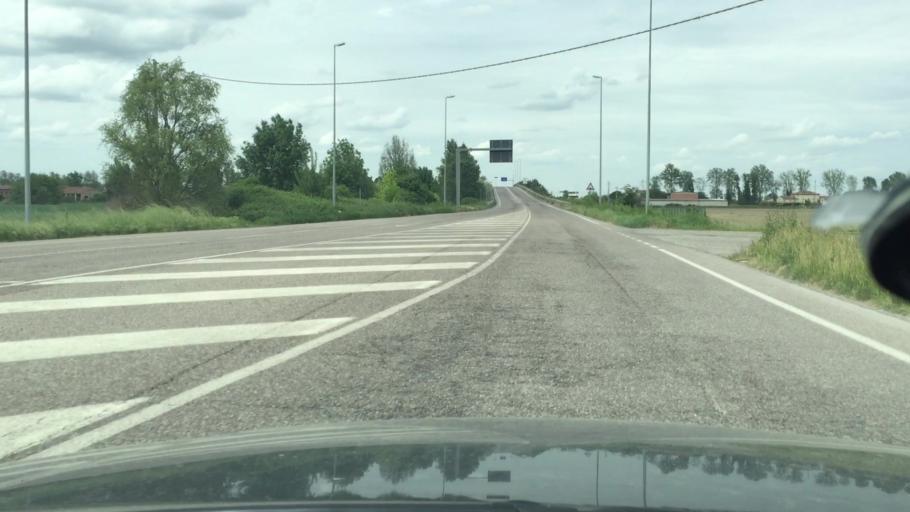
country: IT
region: Emilia-Romagna
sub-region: Provincia di Ferrara
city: Cona
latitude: 44.7992
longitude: 11.7224
